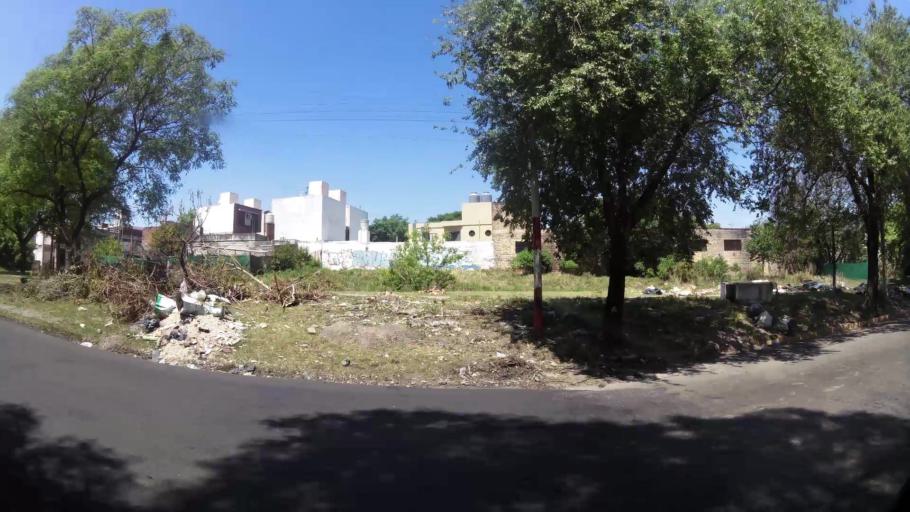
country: AR
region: Cordoba
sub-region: Departamento de Capital
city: Cordoba
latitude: -31.3951
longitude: -64.1935
